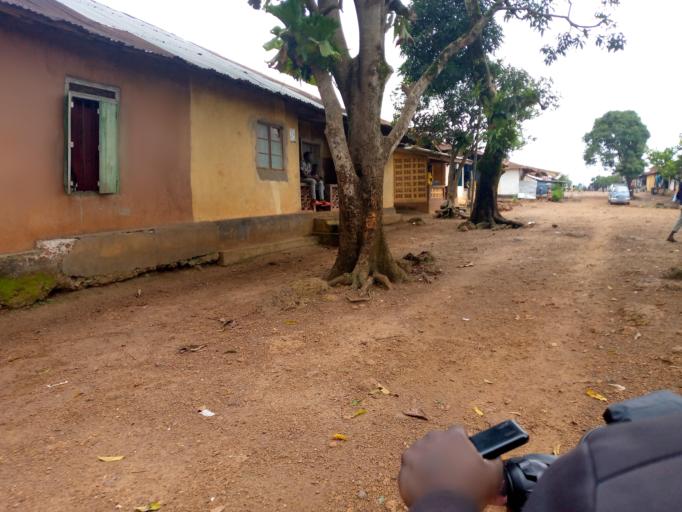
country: SL
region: Eastern Province
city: Kenema
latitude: 7.8723
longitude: -11.1870
